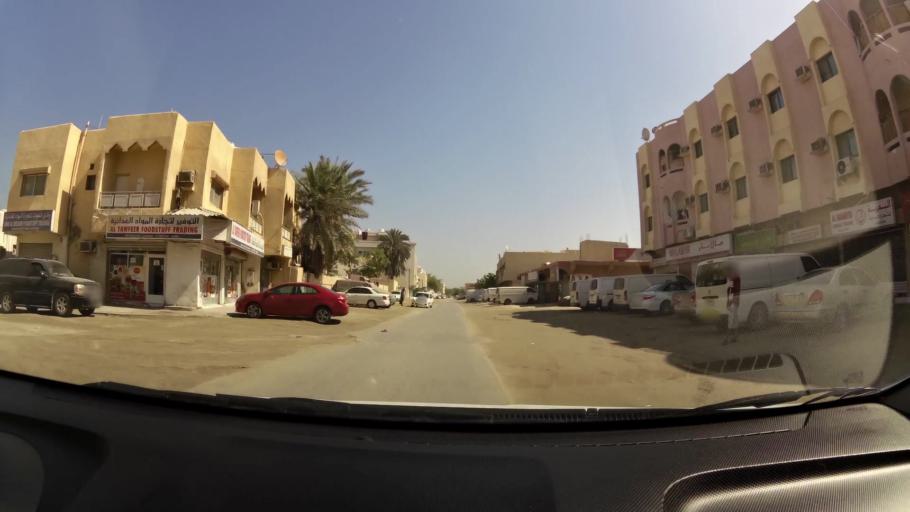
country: AE
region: Ajman
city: Ajman
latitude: 25.4094
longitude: 55.4507
